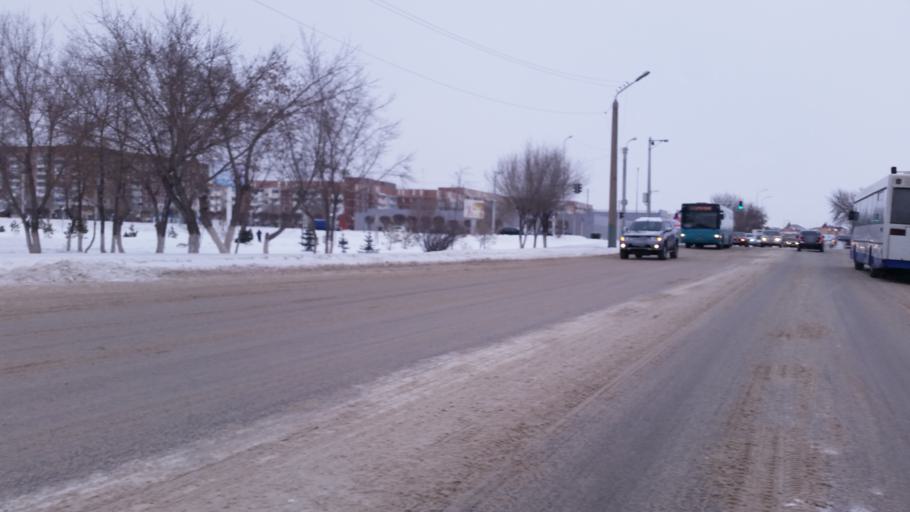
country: KZ
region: Qaraghandy
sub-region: Qaraghandy Qalasy
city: Karagandy
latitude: 49.7767
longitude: 73.1525
